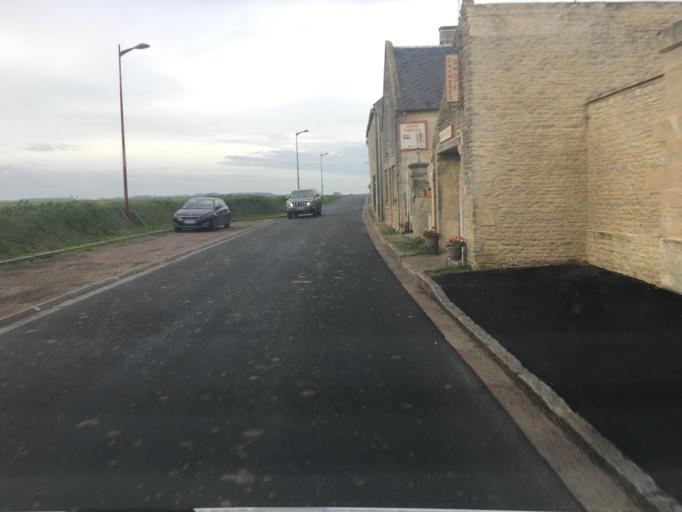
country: FR
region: Lower Normandy
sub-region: Departement du Calvados
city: Ver-sur-Mer
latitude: 49.3274
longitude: -0.5712
